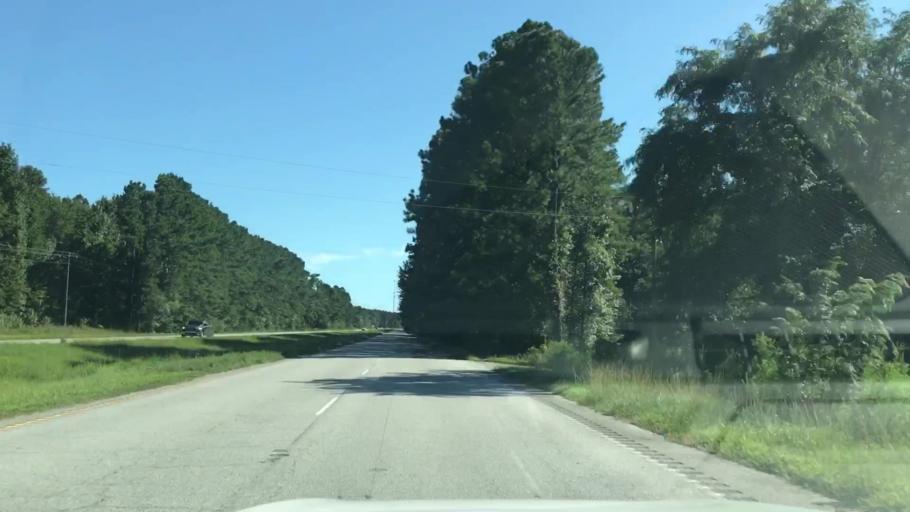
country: US
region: South Carolina
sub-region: Charleston County
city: Awendaw
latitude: 33.0010
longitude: -79.6439
